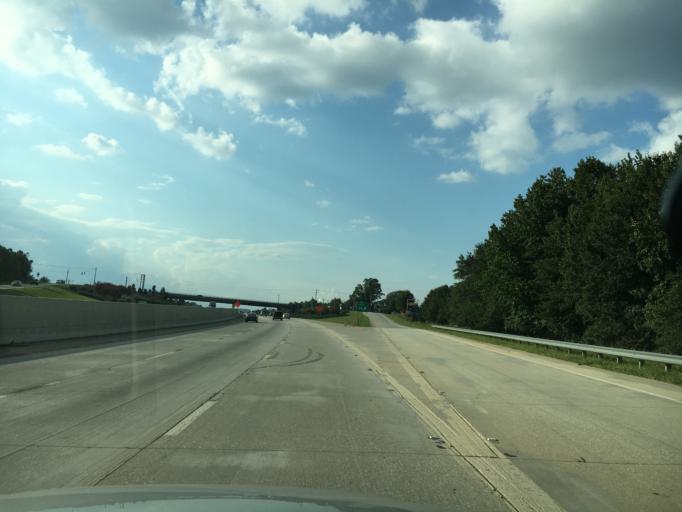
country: US
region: South Carolina
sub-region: Greenville County
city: Mauldin
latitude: 34.8033
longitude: -82.2810
